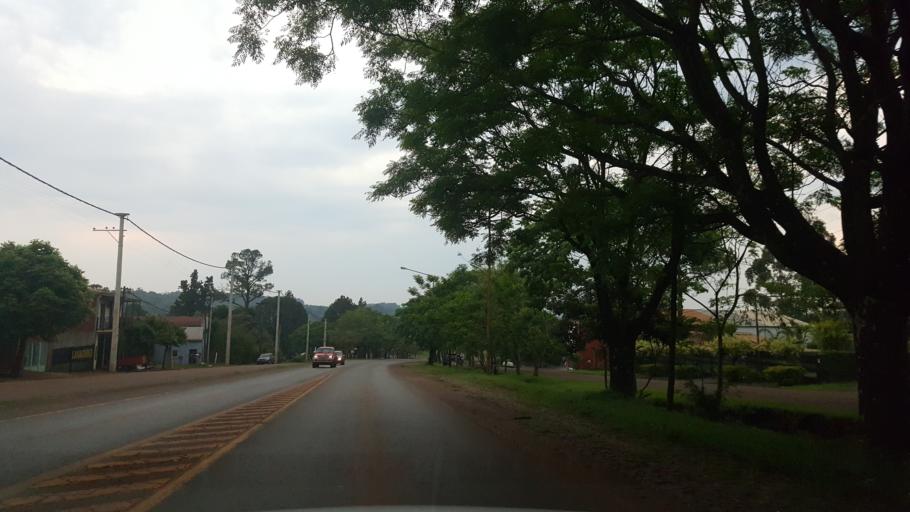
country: AR
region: Misiones
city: Jardin America
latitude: -27.0344
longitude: -55.2243
